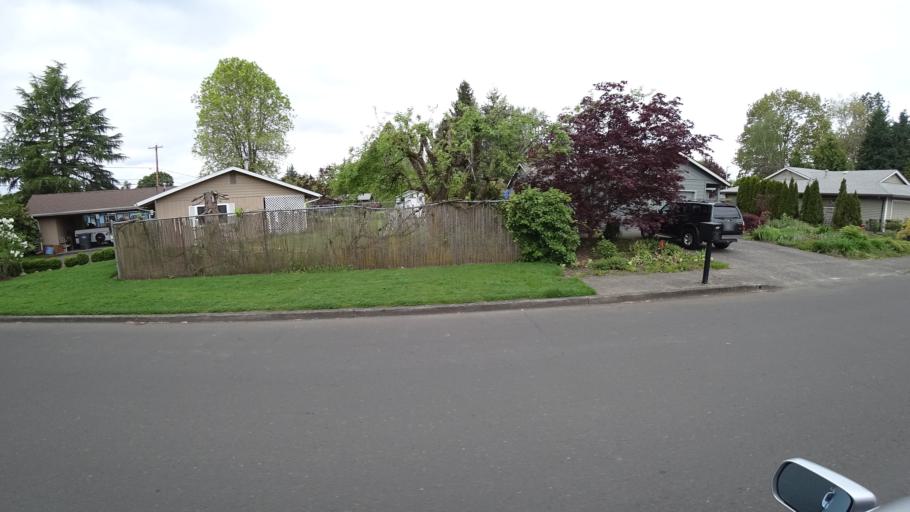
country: US
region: Oregon
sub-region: Washington County
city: Hillsboro
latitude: 45.5331
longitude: -122.9729
